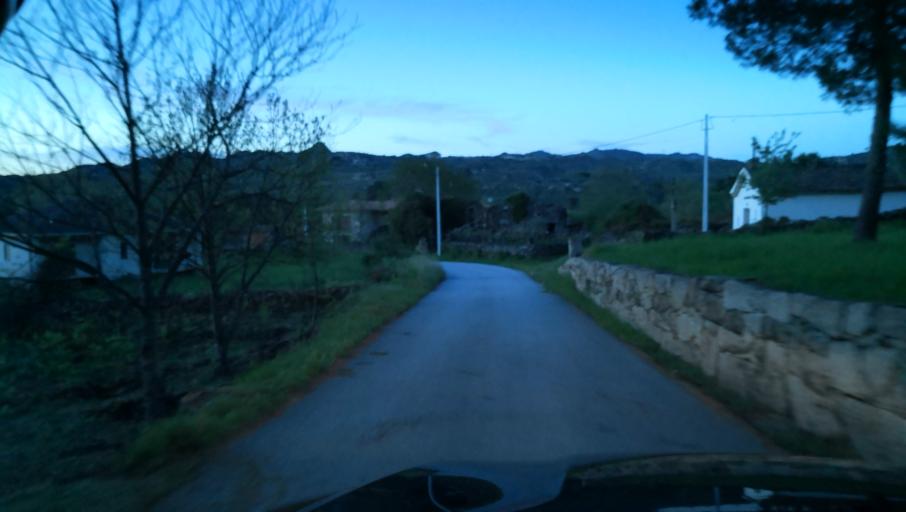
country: PT
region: Vila Real
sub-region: Vila Real
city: Vila Real
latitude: 41.3536
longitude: -7.6897
